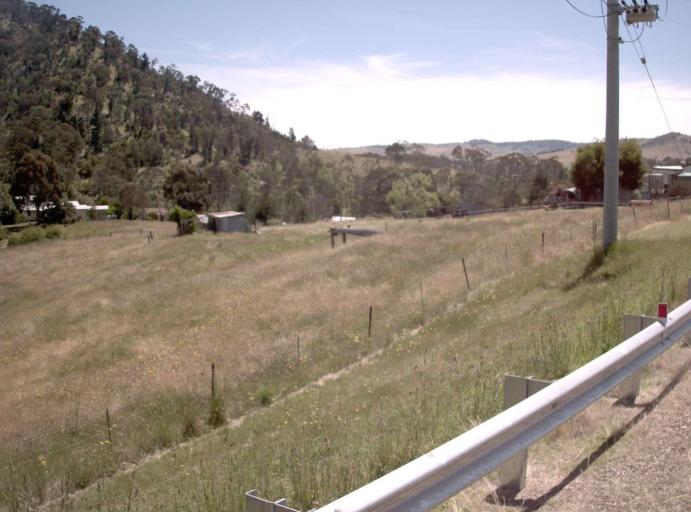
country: AU
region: Victoria
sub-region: Alpine
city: Mount Beauty
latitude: -37.1031
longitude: 147.5841
